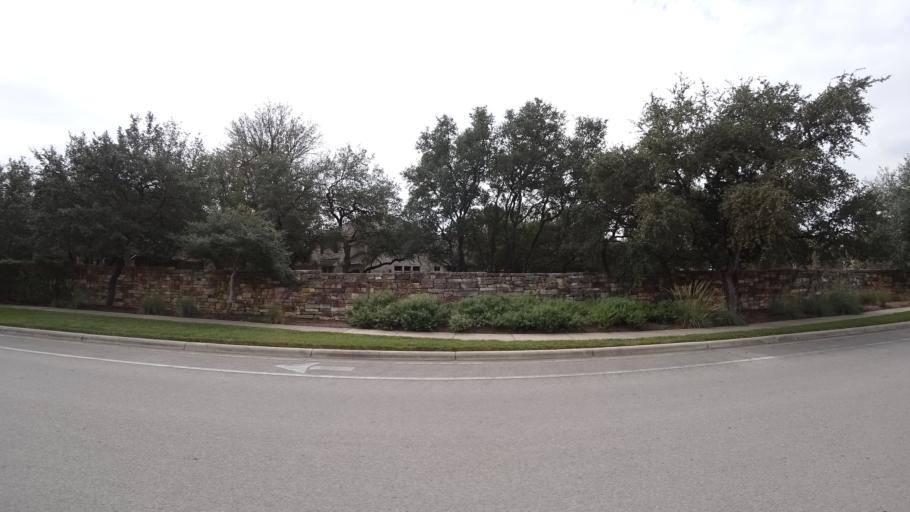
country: US
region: Texas
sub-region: Travis County
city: Shady Hollow
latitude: 30.2000
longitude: -97.9177
